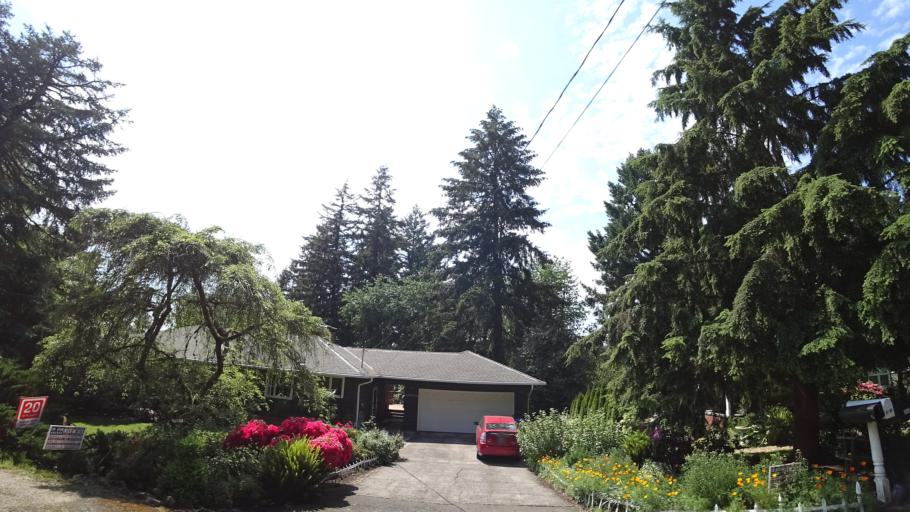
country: US
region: Oregon
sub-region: Washington County
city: Metzger
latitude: 45.4501
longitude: -122.7317
